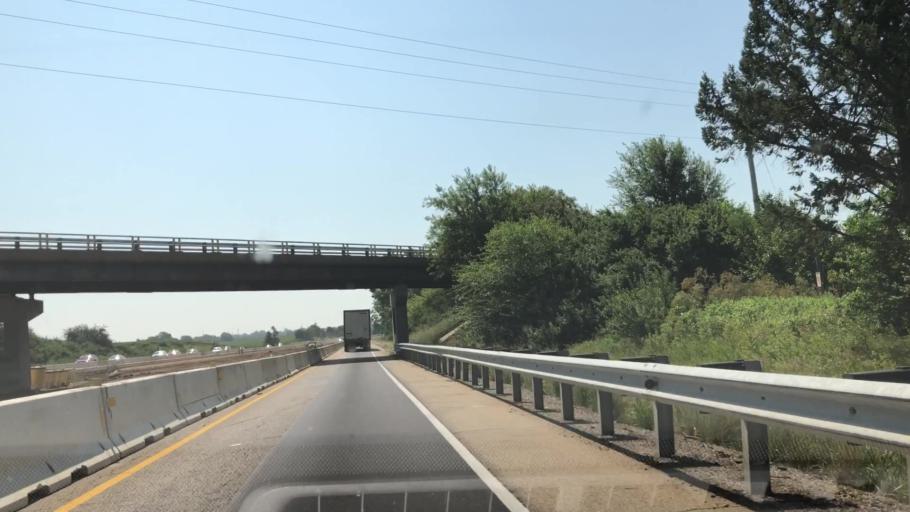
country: US
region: Illinois
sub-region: McLean County
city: Danvers
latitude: 40.5936
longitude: -89.1555
